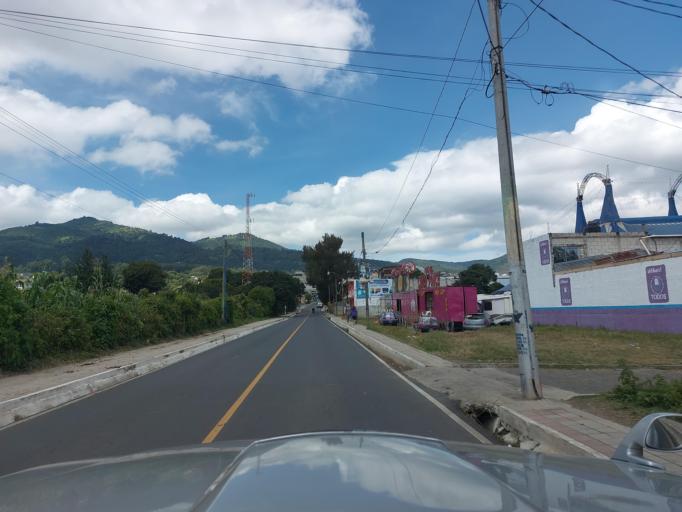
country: GT
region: Chimaltenango
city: San Andres Itzapa
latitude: 14.6239
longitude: -90.8350
